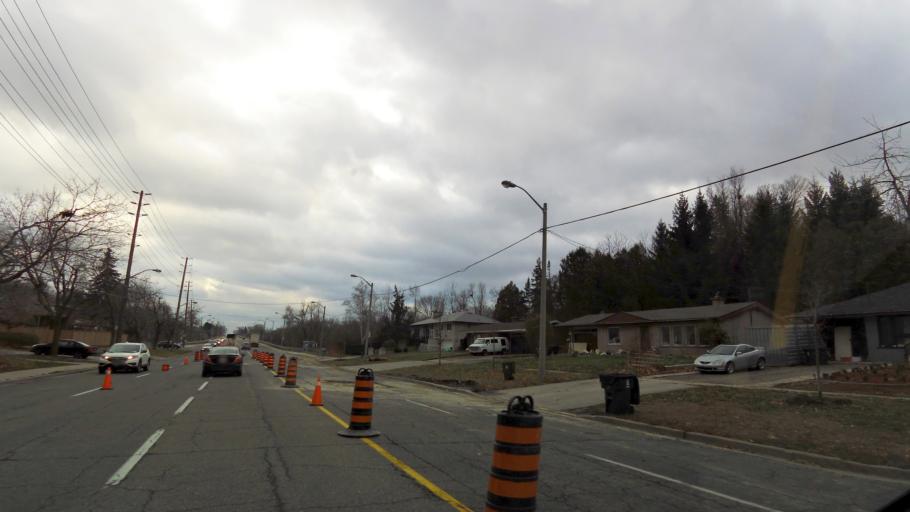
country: CA
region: Ontario
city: Etobicoke
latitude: 43.7329
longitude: -79.5634
